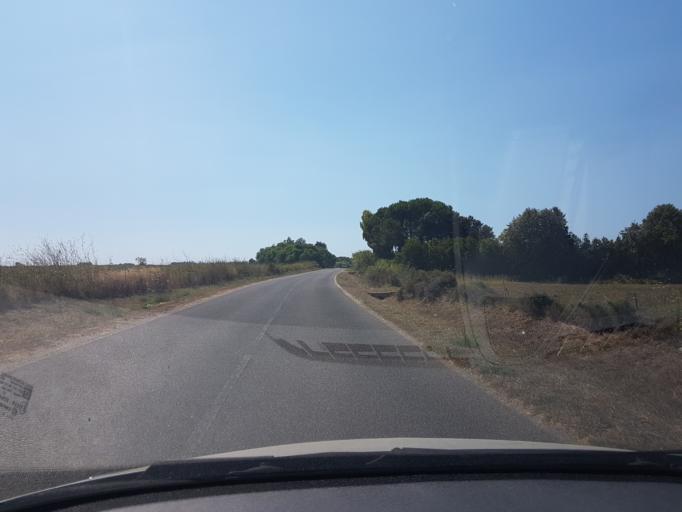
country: IT
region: Sardinia
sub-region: Provincia di Oristano
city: Riola Sardo
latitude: 40.0006
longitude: 8.5112
